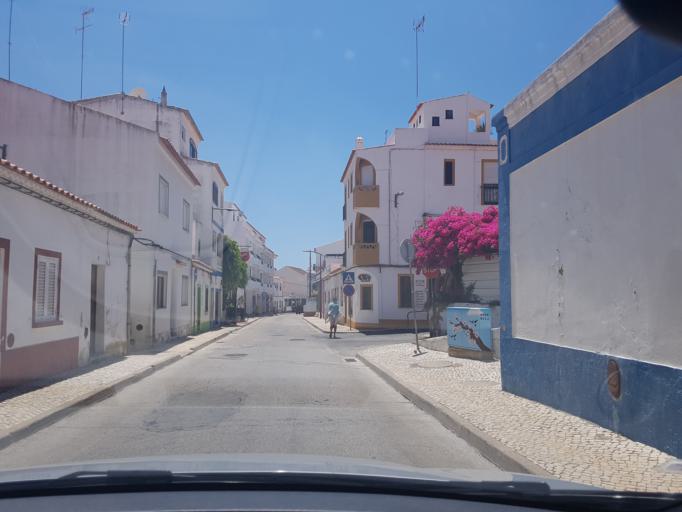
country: PT
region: Faro
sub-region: Lagoa
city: Carvoeiro
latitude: 37.0997
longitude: -8.4696
